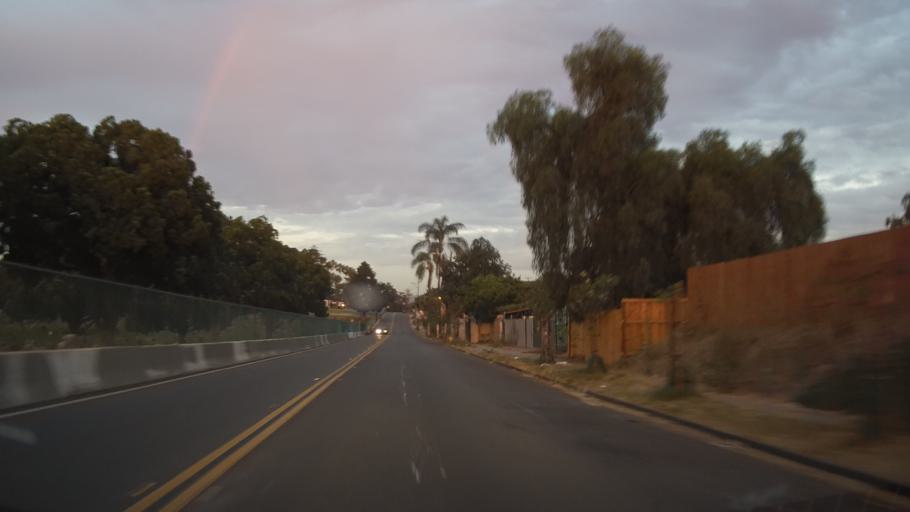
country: US
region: California
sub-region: San Diego County
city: National City
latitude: 32.7048
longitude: -117.1142
